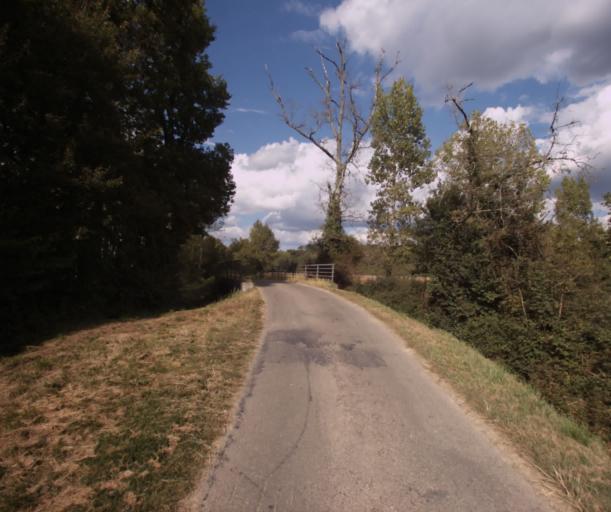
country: FR
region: Midi-Pyrenees
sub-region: Departement du Gers
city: Cazaubon
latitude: 43.9124
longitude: -0.0513
